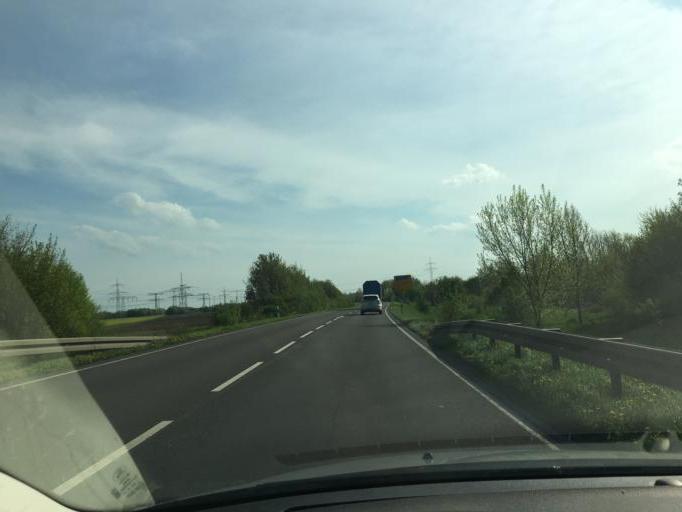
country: DE
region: Saxony-Anhalt
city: Meitzendorf
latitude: 52.2099
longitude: 11.5470
